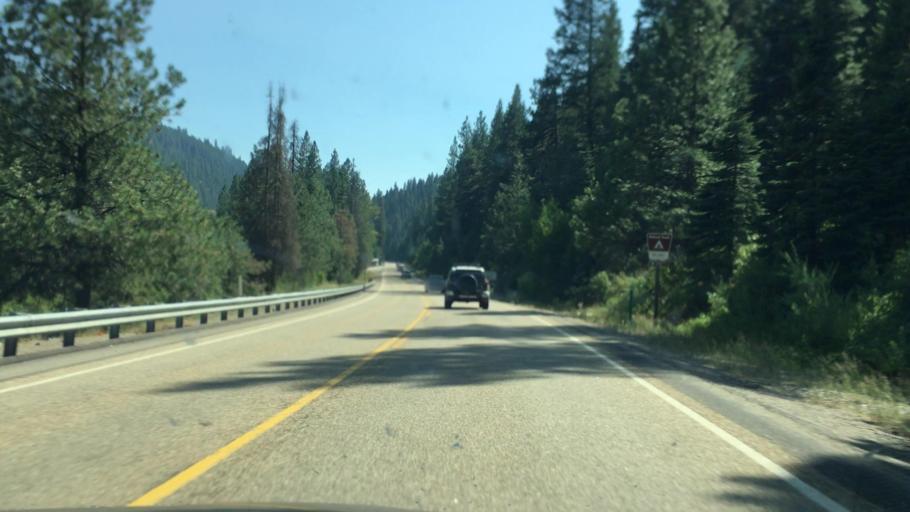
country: US
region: Idaho
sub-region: Valley County
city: Cascade
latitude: 44.2224
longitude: -116.1068
